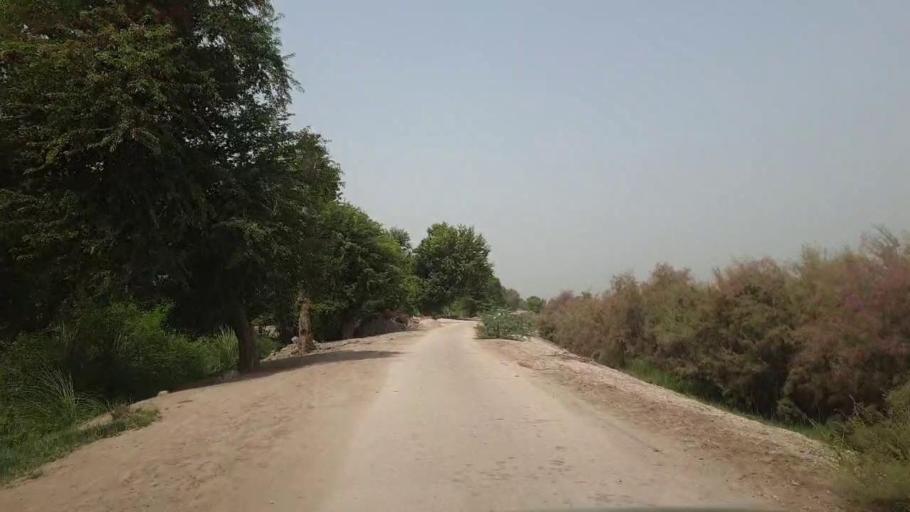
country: PK
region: Sindh
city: Gambat
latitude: 27.4408
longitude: 68.4982
